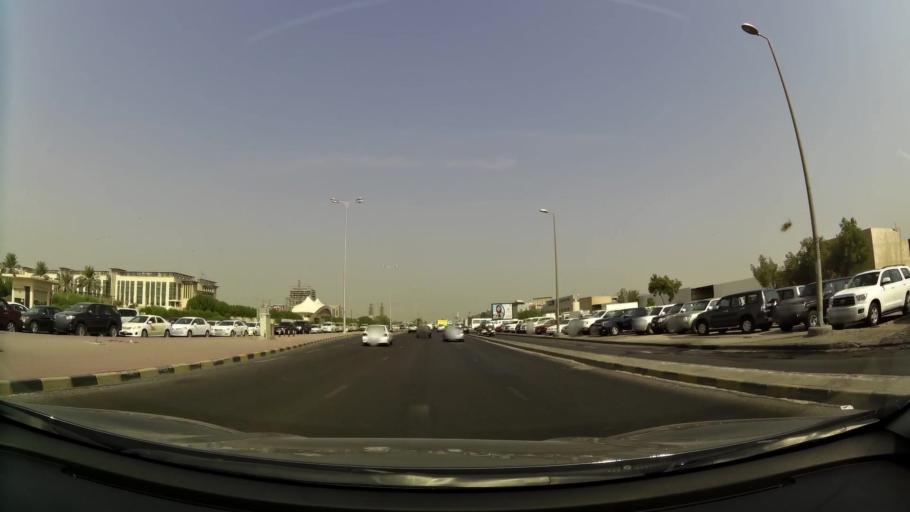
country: KW
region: Al Asimah
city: Ar Rabiyah
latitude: 29.3035
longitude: 47.9274
